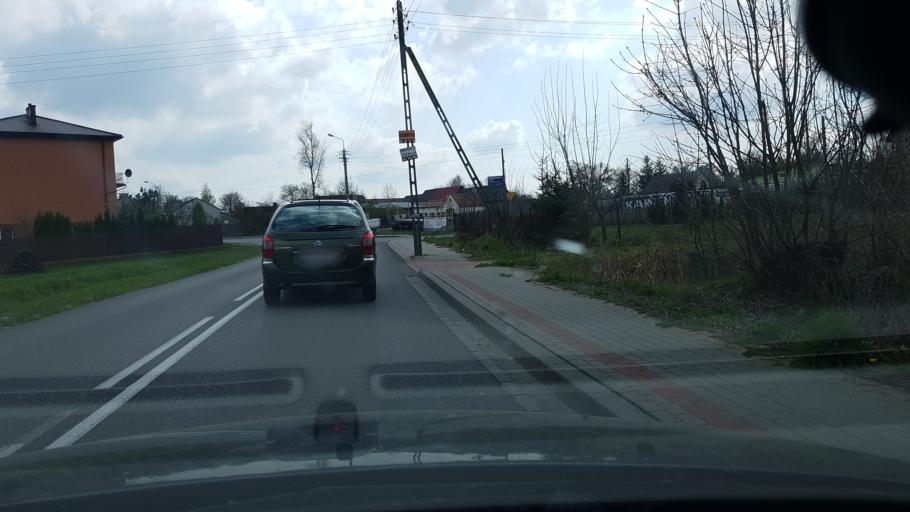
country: PL
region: Masovian Voivodeship
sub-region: Powiat minski
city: Kaluszyn
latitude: 52.1974
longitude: 21.8080
